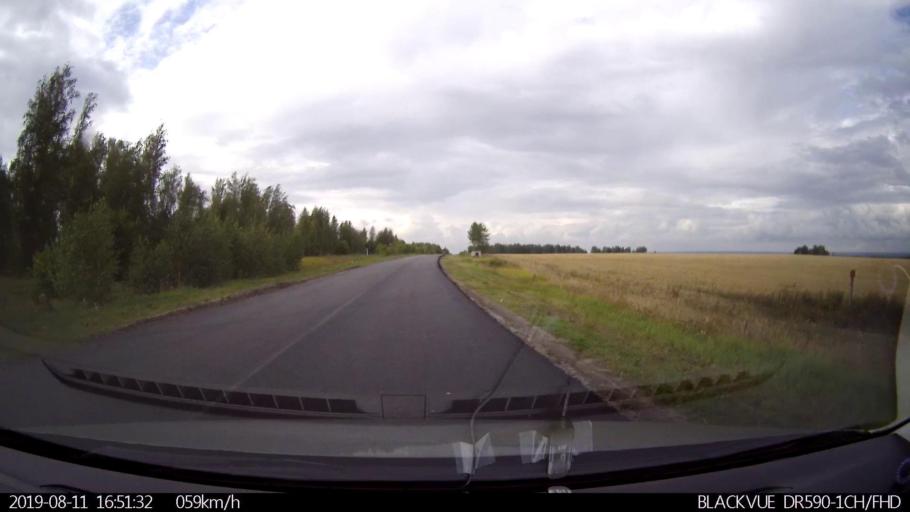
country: RU
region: Ulyanovsk
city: Mayna
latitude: 54.2380
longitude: 47.6767
